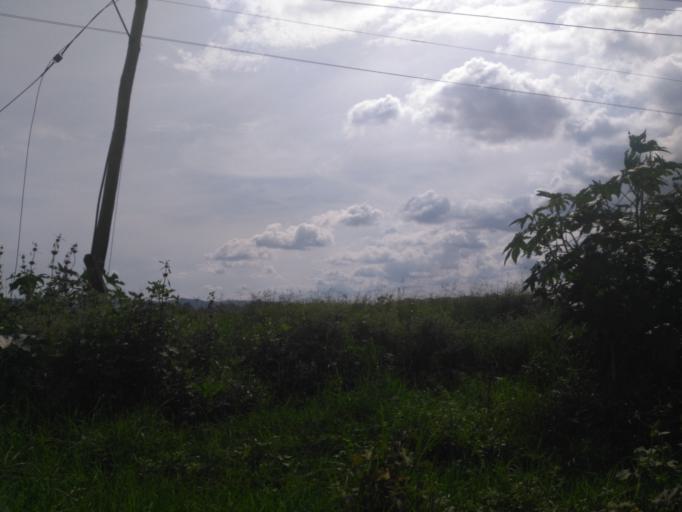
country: UG
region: Eastern Region
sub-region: Jinja District
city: Jinja
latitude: 0.4247
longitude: 33.2210
